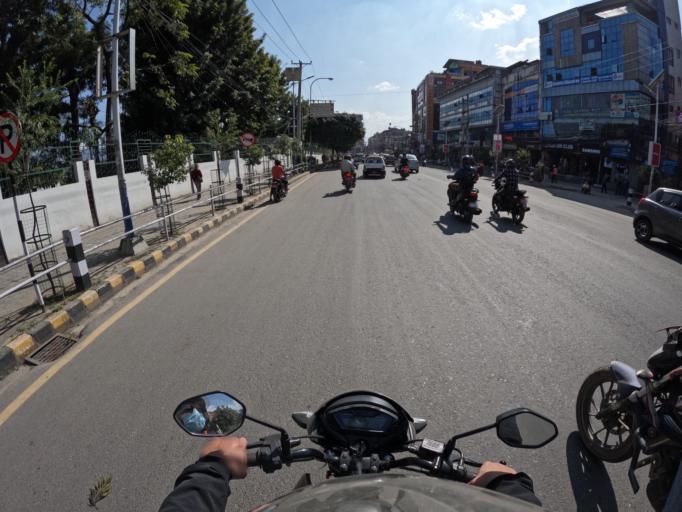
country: NP
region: Central Region
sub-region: Bagmati Zone
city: Kathmandu
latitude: 27.6897
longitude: 85.3359
